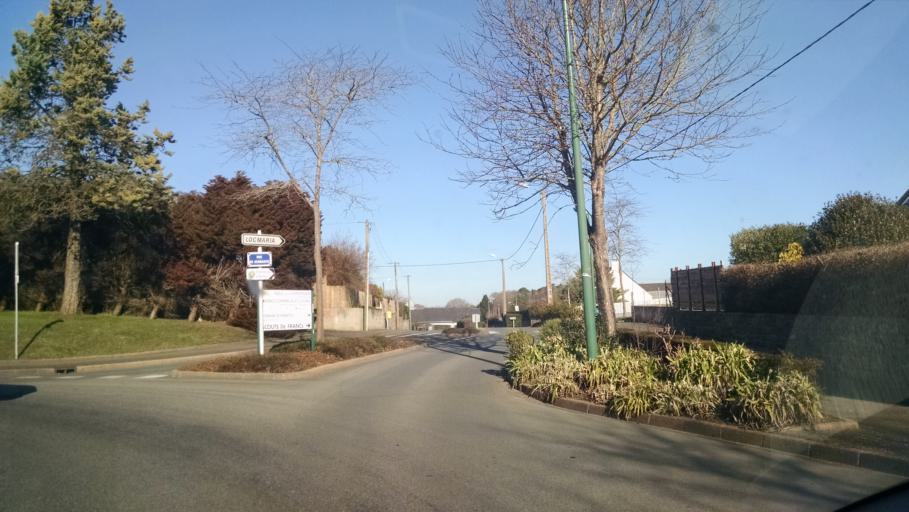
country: FR
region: Brittany
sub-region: Departement du Morbihan
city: Guidel-Plage
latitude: 47.7927
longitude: -3.4915
